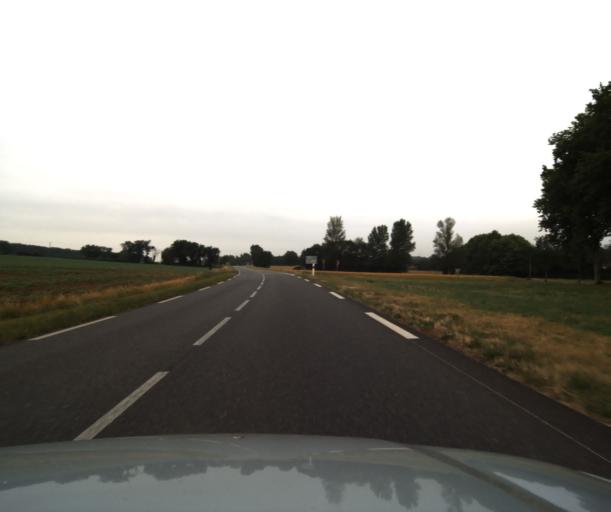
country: FR
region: Midi-Pyrenees
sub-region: Departement du Gers
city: Aubiet
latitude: 43.6914
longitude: 0.8295
